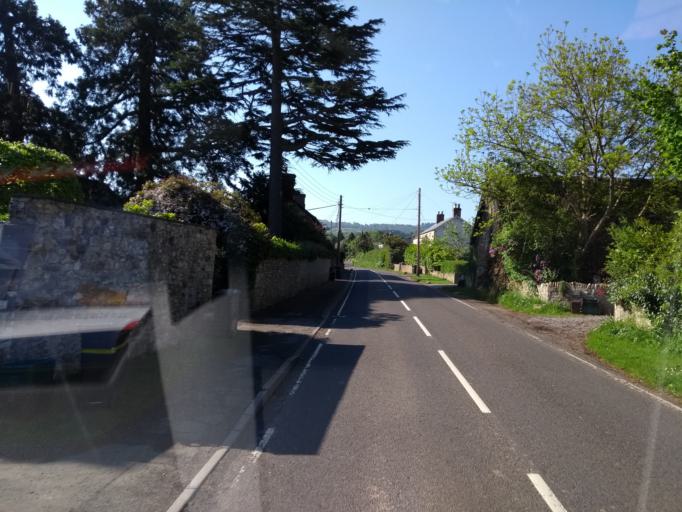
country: GB
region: England
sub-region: Somerset
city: Taunton
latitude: 50.9705
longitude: -3.0953
